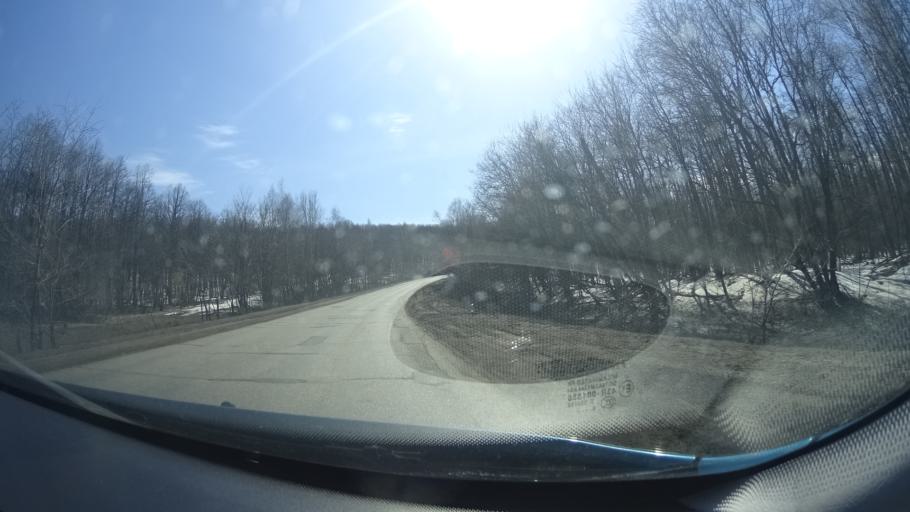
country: RU
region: Bashkortostan
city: Oktyabr'skiy
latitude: 54.4752
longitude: 53.5780
